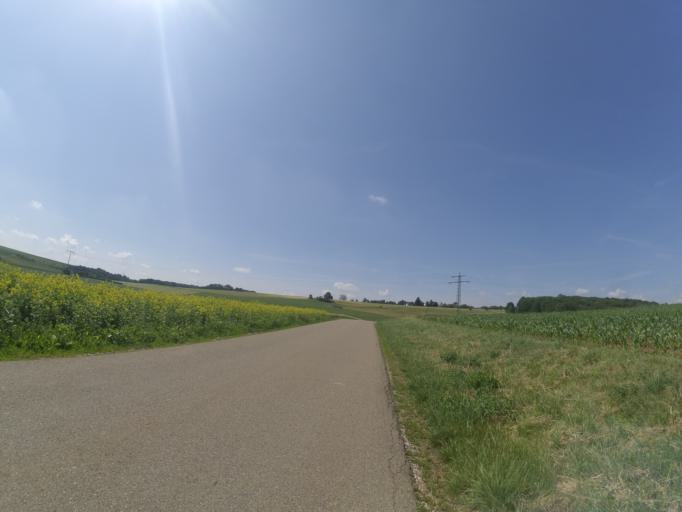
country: DE
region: Baden-Wuerttemberg
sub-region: Tuebingen Region
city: Bernstadt
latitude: 48.4800
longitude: 10.0229
